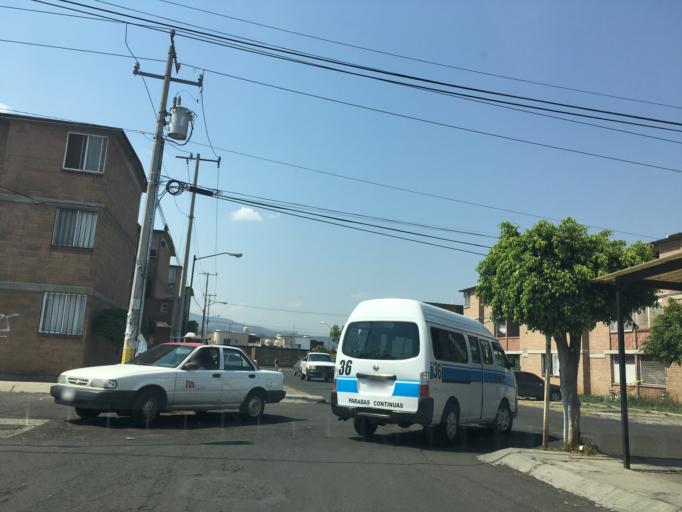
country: MX
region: Michoacan
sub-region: Morelia
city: Morelos
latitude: 19.6725
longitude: -101.2253
